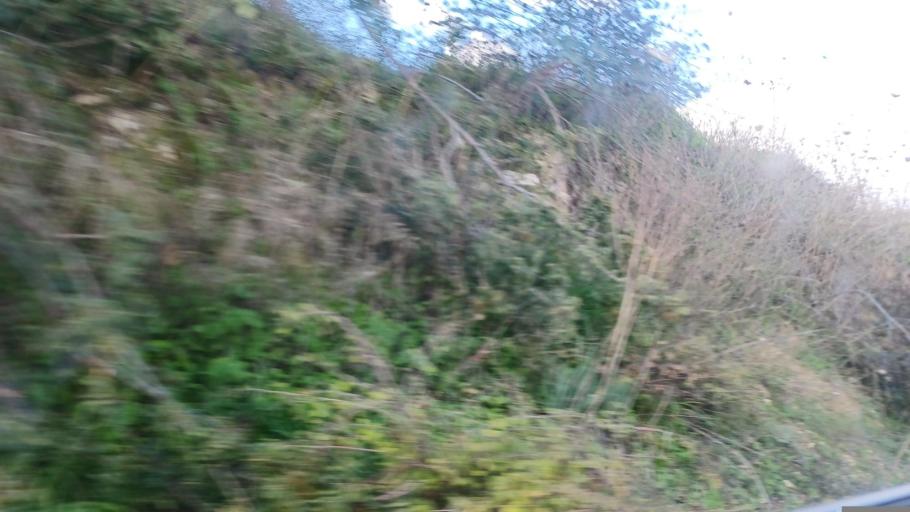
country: CY
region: Pafos
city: Mesogi
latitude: 34.8327
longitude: 32.5517
